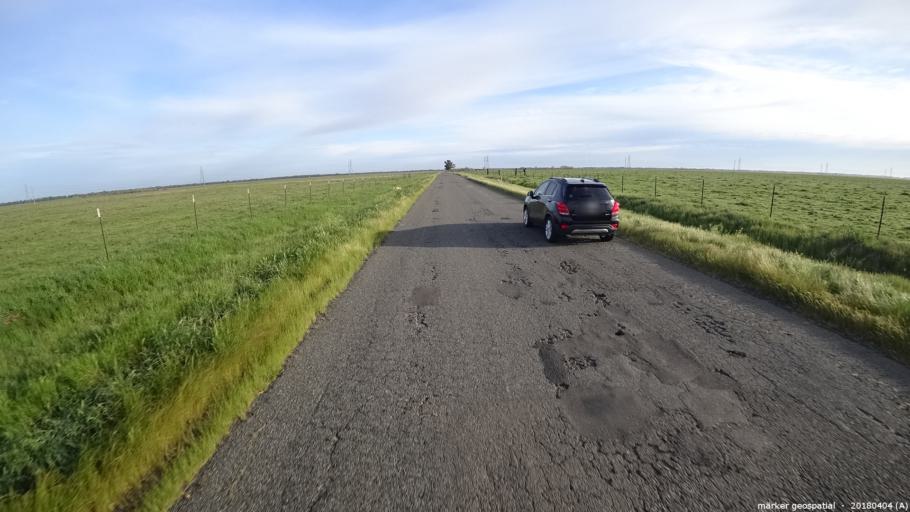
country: US
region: California
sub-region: Sacramento County
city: Herald
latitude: 38.3430
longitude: -121.2976
